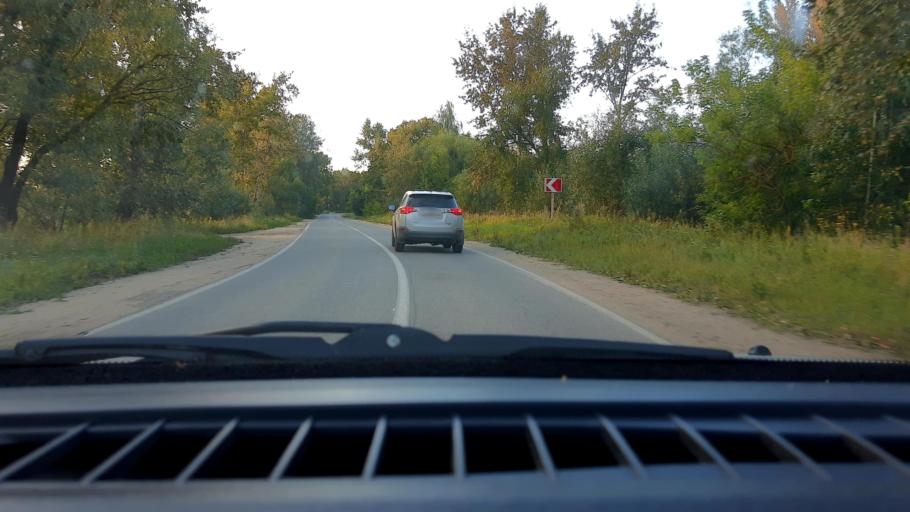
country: RU
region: Nizjnij Novgorod
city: Bor
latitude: 56.3506
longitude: 44.0528
